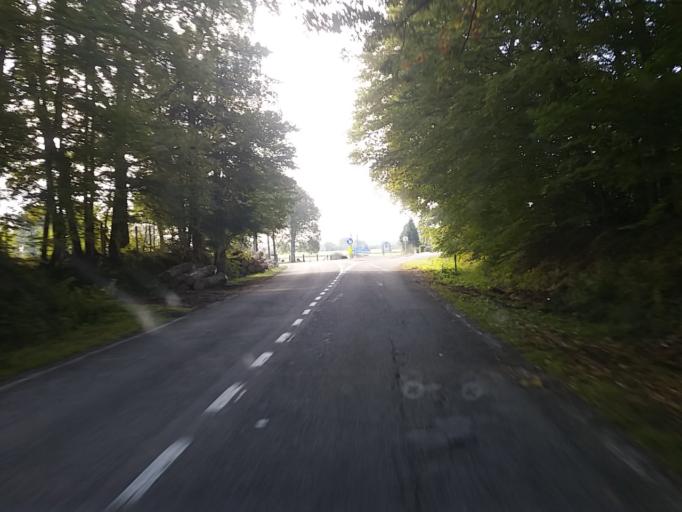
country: BE
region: Wallonia
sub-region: Province du Luxembourg
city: Herbeumont
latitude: 49.7367
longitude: 5.2275
